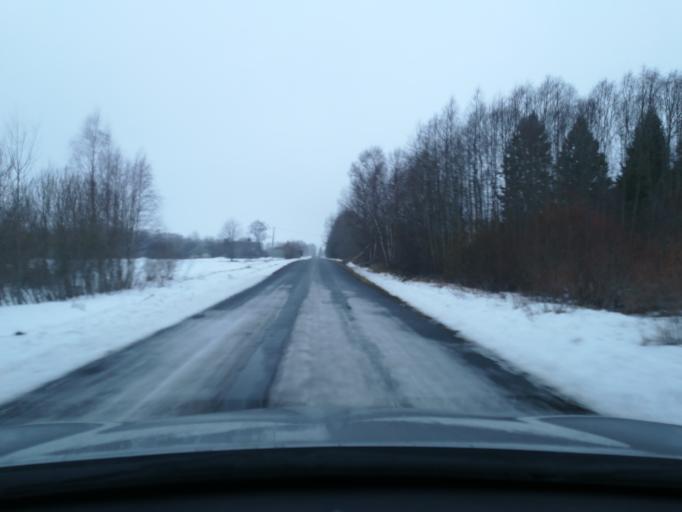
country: EE
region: Harju
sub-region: Raasiku vald
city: Raasiku
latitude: 59.3423
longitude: 25.2256
